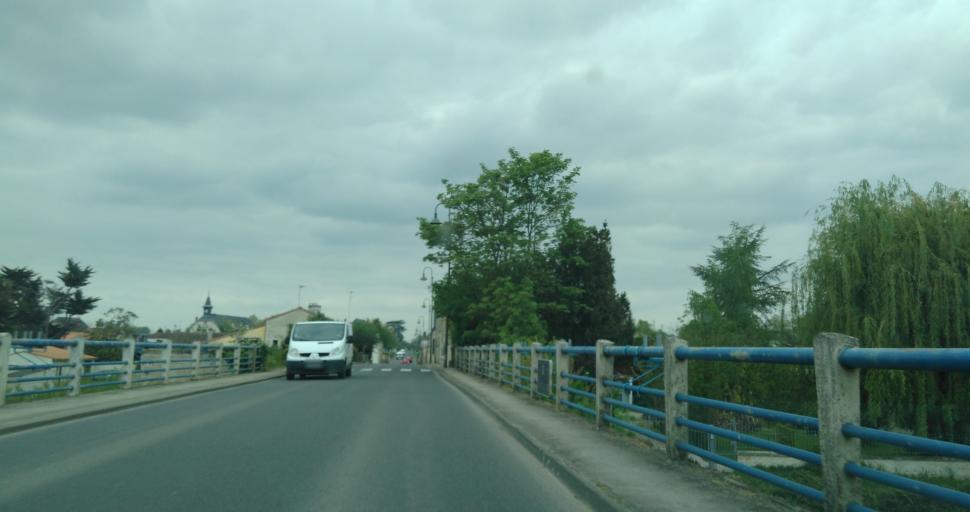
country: FR
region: Poitou-Charentes
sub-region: Departement des Deux-Sevres
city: Coulon
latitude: 46.3225
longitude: -0.5812
